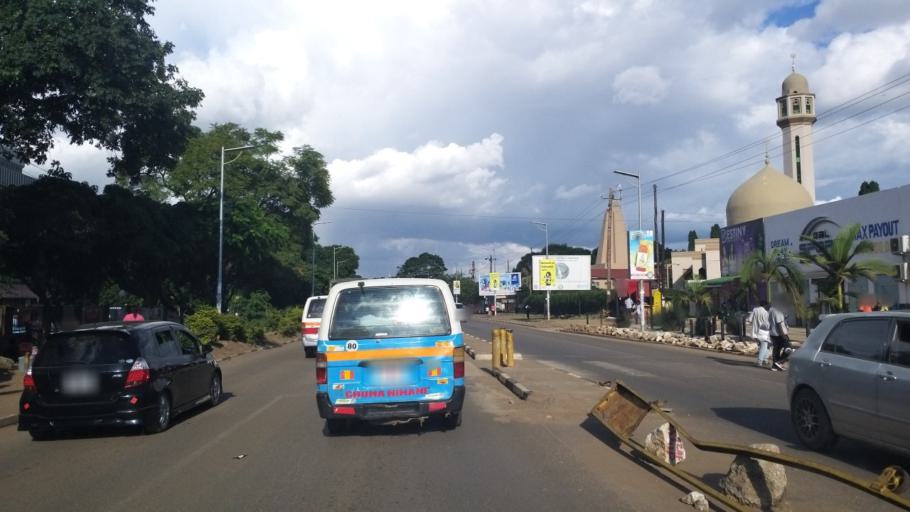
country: ZM
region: Lusaka
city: Lusaka
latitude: -15.4242
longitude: 28.2879
